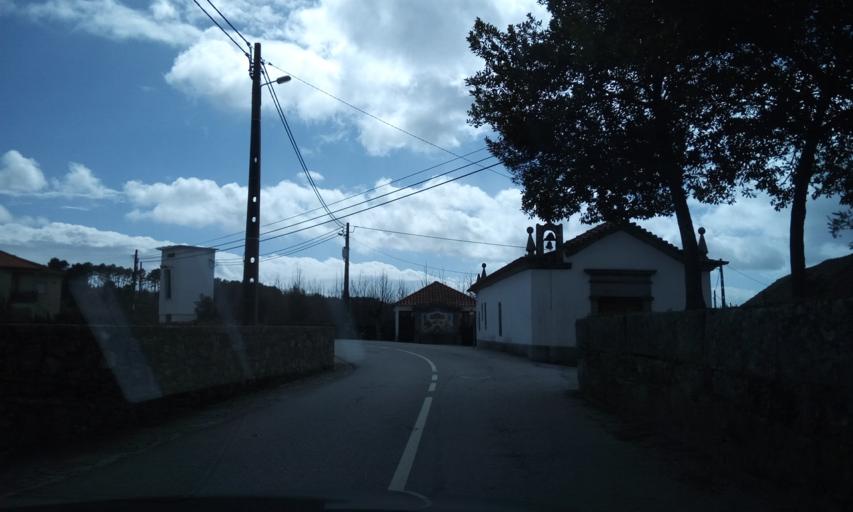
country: PT
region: Guarda
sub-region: Fornos de Algodres
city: Fornos de Algodres
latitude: 40.6475
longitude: -7.5477
